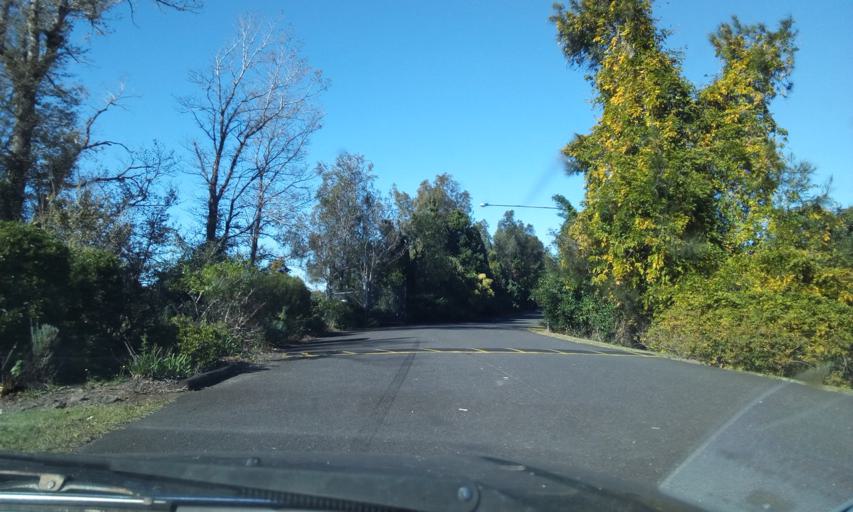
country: AU
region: New South Wales
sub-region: Wollongong
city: Dapto
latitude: -34.5263
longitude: 150.7745
